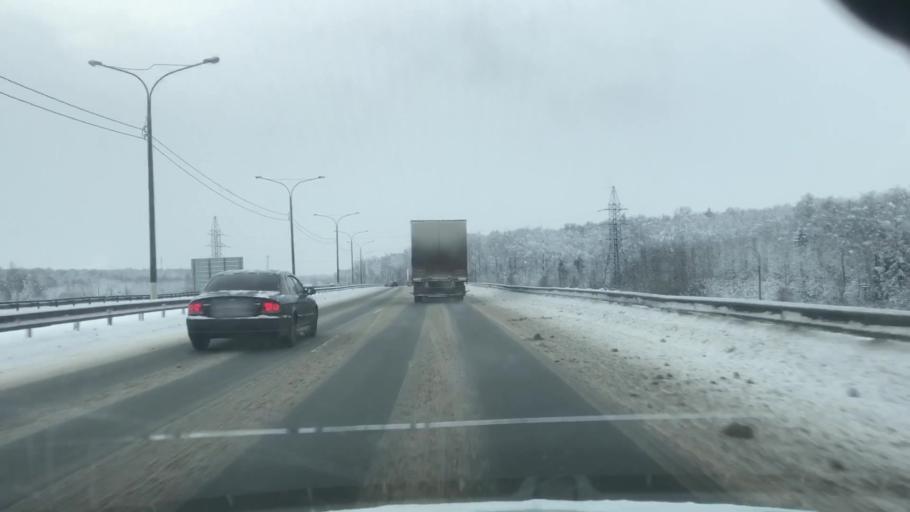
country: RU
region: Moskovskaya
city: Mikhnevo
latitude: 55.1424
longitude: 37.9315
